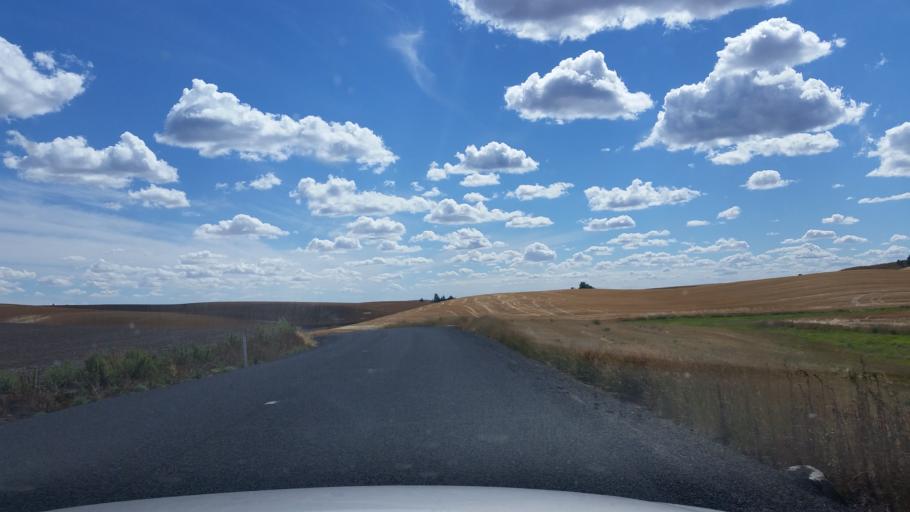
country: US
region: Washington
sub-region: Spokane County
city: Cheney
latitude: 47.4971
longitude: -117.6201
